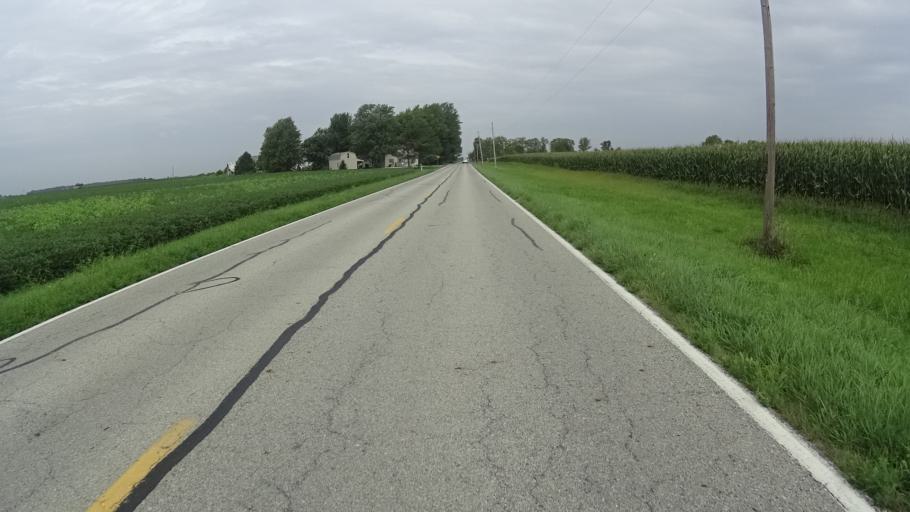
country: US
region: Indiana
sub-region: Madison County
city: Lapel
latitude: 40.0392
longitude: -85.8024
